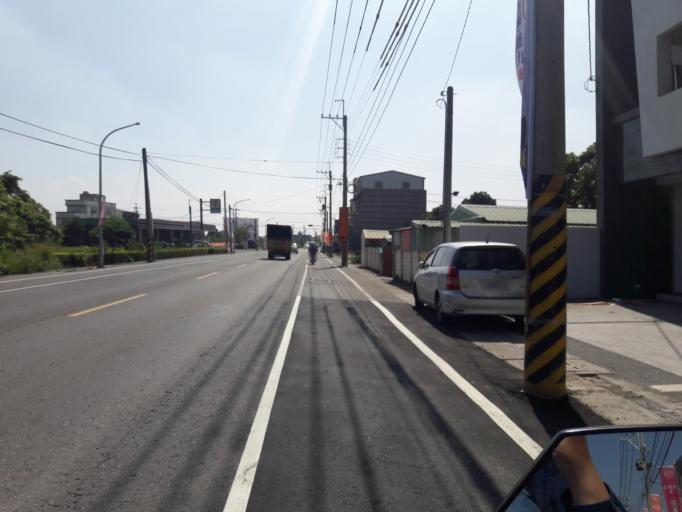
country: TW
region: Taiwan
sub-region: Chiayi
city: Jiayi Shi
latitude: 23.5377
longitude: 120.4249
